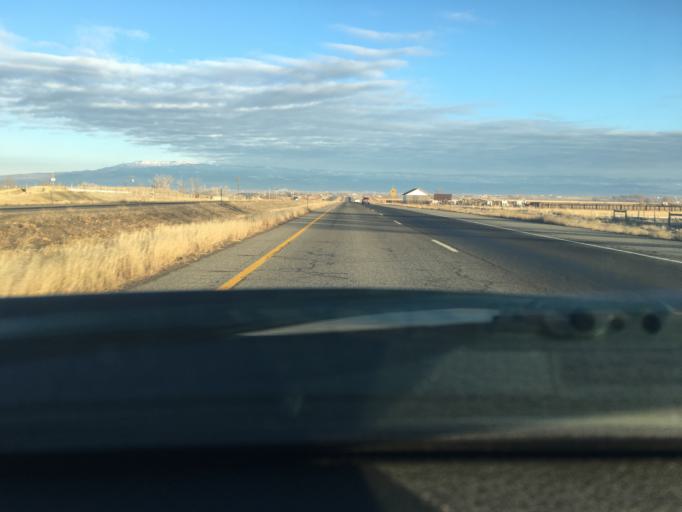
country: US
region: Colorado
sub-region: Montrose County
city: Olathe
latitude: 38.6317
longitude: -107.9858
